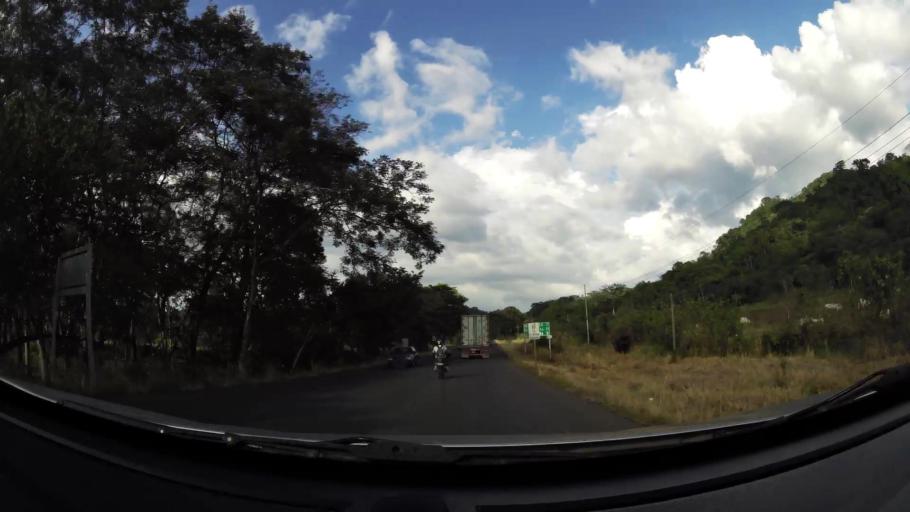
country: CR
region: Puntarenas
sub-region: Canton de Garabito
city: Jaco
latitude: 9.7594
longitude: -84.6170
